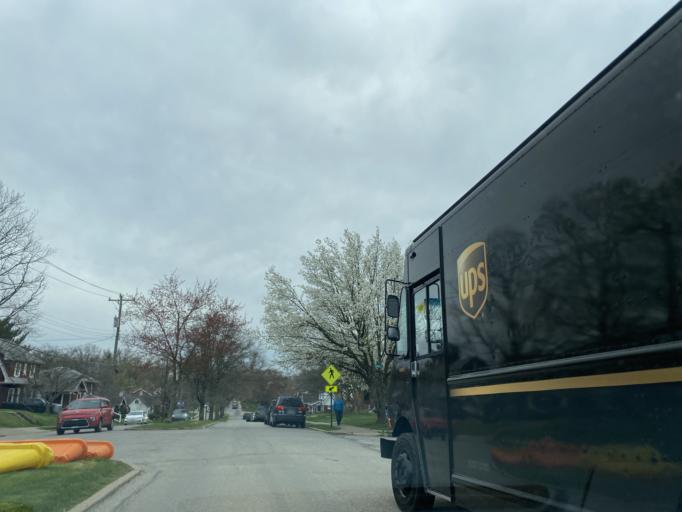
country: US
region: Kentucky
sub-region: Campbell County
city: Fort Thomas
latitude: 39.0907
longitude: -84.4476
